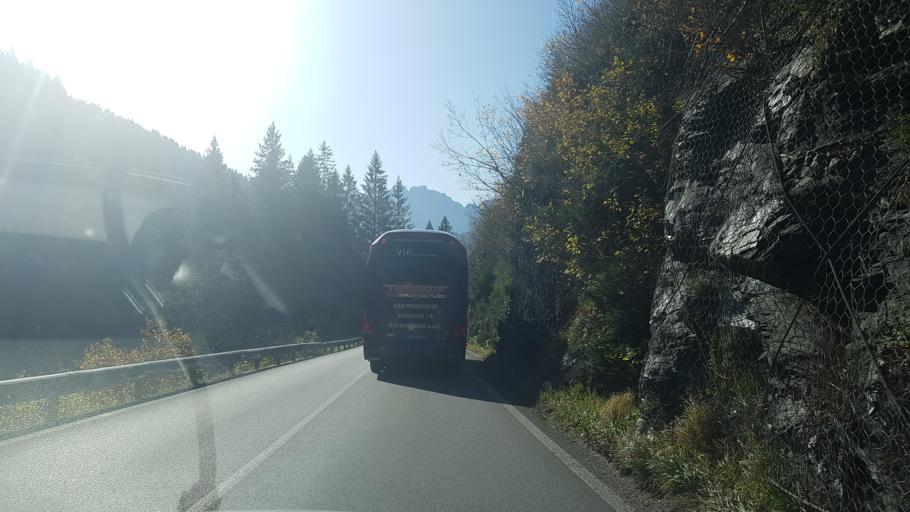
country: IT
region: Veneto
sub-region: Provincia di Belluno
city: Candide
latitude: 46.5969
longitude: 12.5232
